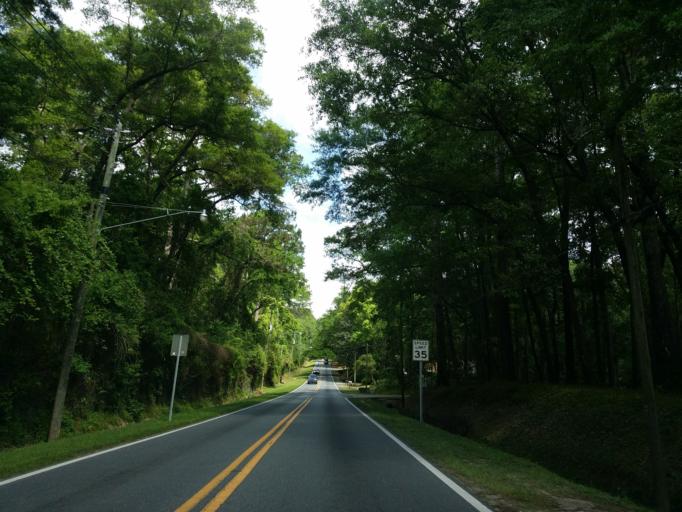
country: US
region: Florida
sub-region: Leon County
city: Tallahassee
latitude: 30.4200
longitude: -84.2739
